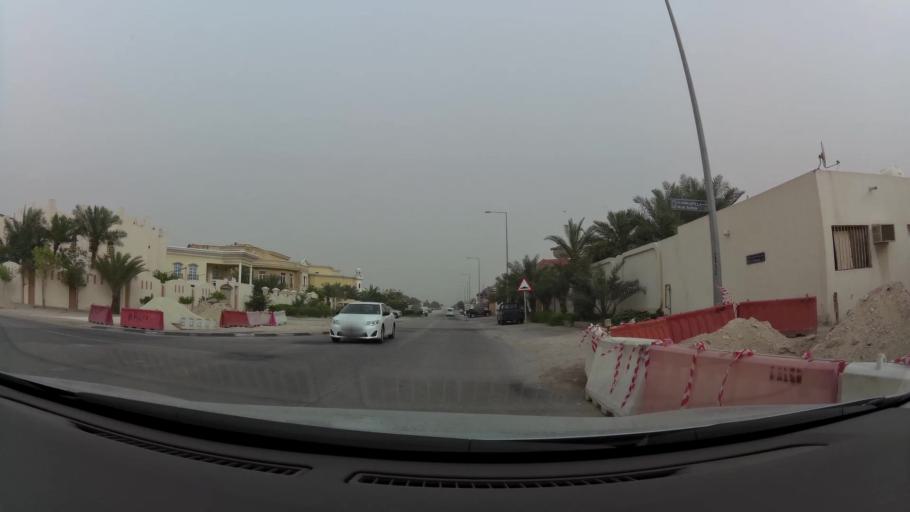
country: QA
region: Baladiyat ad Dawhah
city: Doha
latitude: 25.2509
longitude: 51.4961
